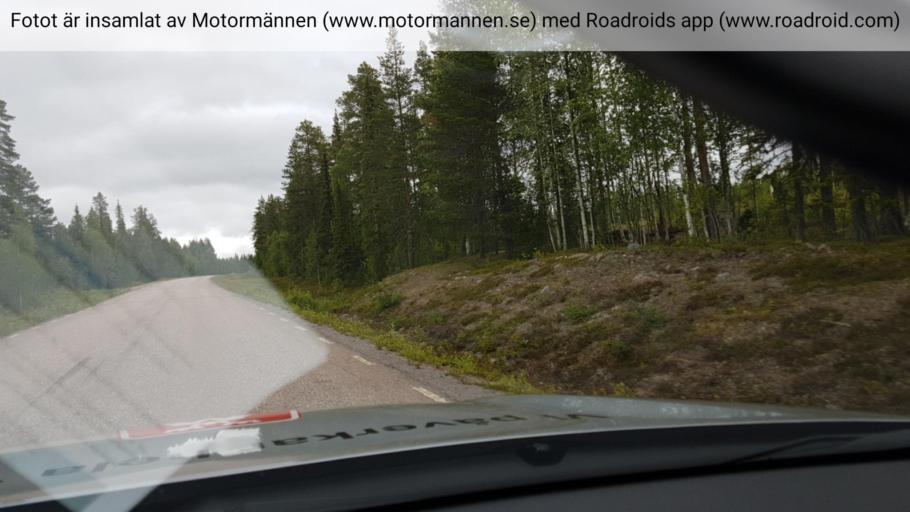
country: SE
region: Norrbotten
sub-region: Overkalix Kommun
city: OEverkalix
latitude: 67.0262
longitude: 22.0041
